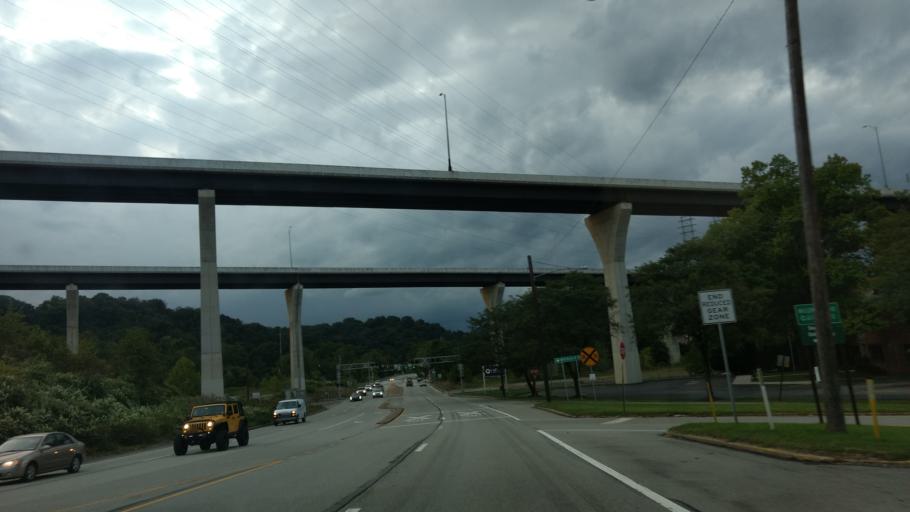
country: US
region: Pennsylvania
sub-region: Allegheny County
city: Jefferson Hills
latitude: 40.2906
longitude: -79.9133
